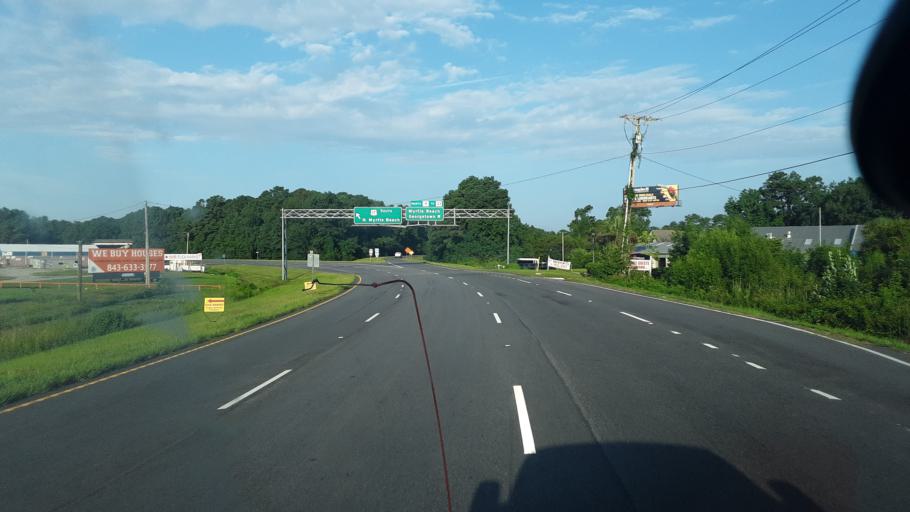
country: US
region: South Carolina
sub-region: Horry County
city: Little River
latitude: 33.8651
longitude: -78.6540
